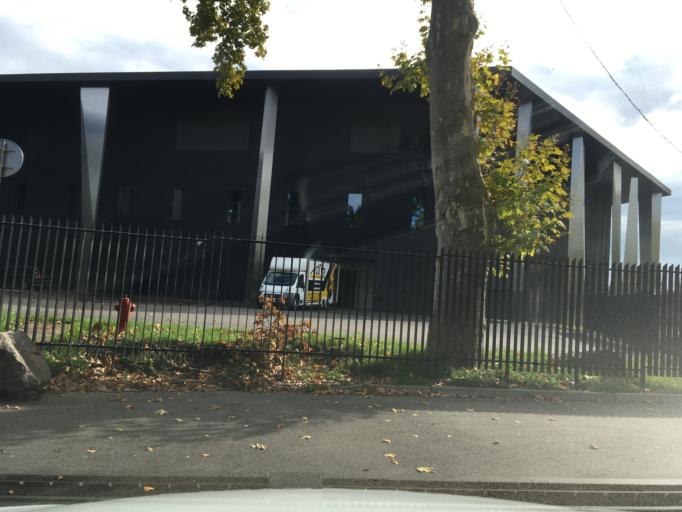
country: FR
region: Alsace
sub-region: Departement du Bas-Rhin
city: Schiltigheim
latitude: 48.5981
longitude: 7.7559
